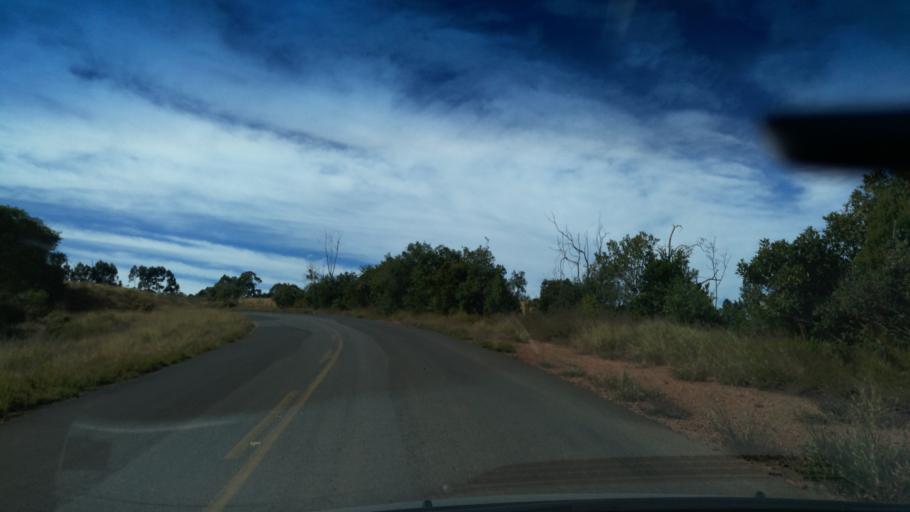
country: BR
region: Minas Gerais
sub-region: Andradas
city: Andradas
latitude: -22.0441
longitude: -46.3421
